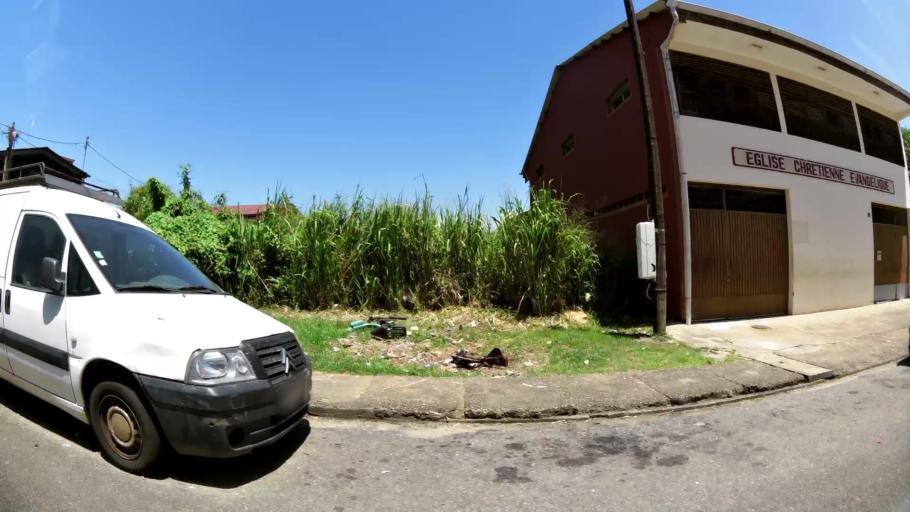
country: GF
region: Guyane
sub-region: Guyane
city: Cayenne
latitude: 4.9348
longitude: -52.3300
